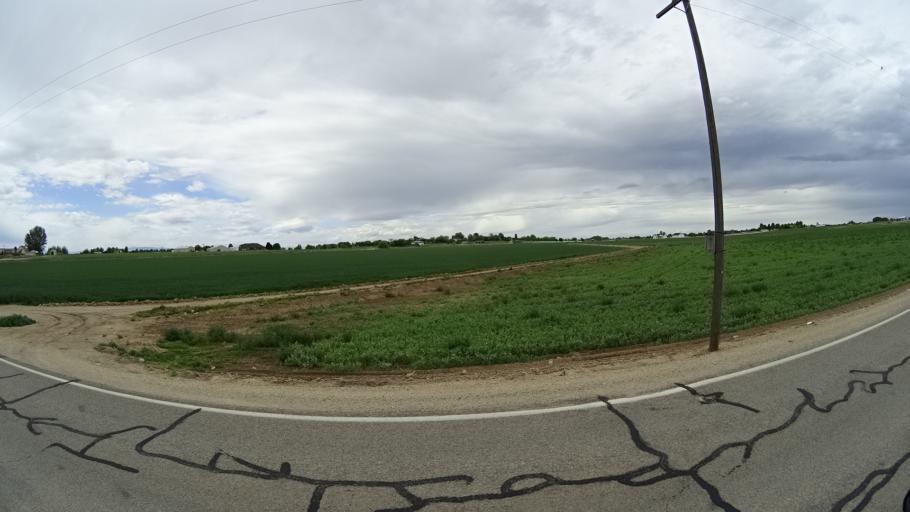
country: US
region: Idaho
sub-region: Ada County
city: Meridian
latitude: 43.5636
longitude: -116.4138
